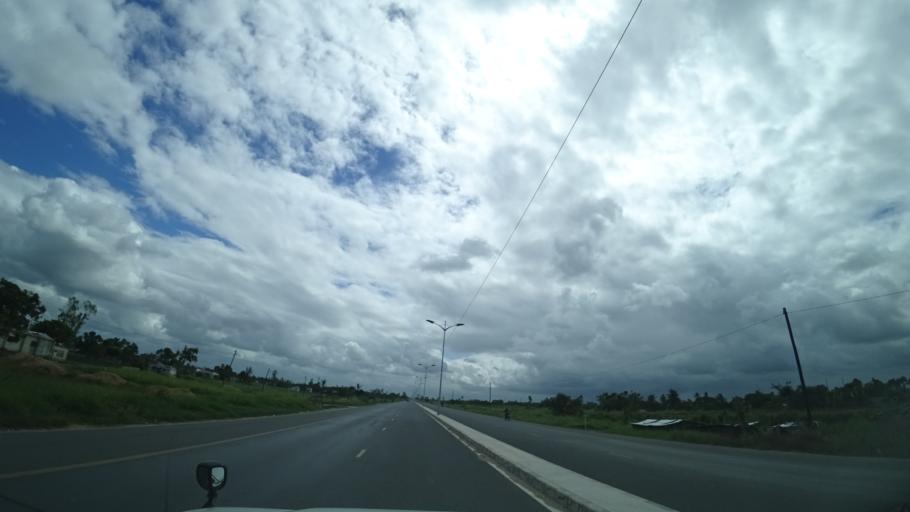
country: MZ
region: Sofala
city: Dondo
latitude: -19.6045
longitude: 34.7423
